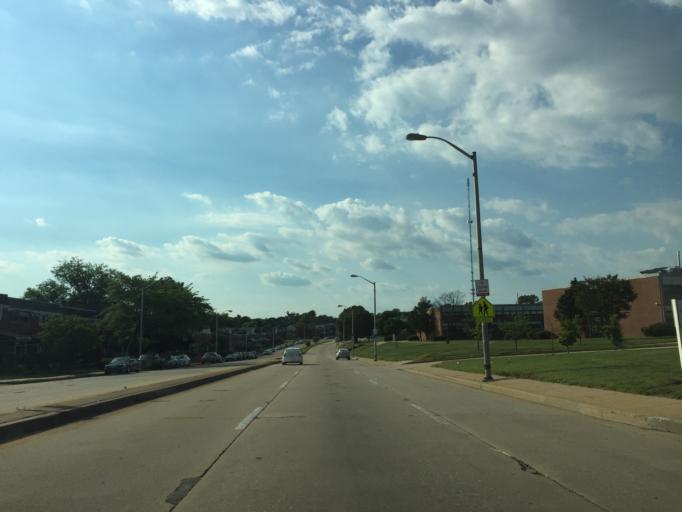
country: US
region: Maryland
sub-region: Baltimore County
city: Rosedale
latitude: 39.3185
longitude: -76.5464
